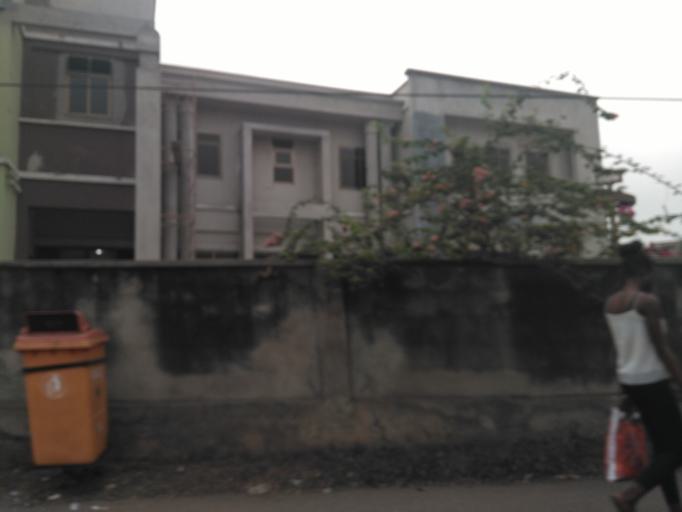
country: GH
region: Ashanti
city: Kumasi
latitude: 6.7033
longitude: -1.6139
